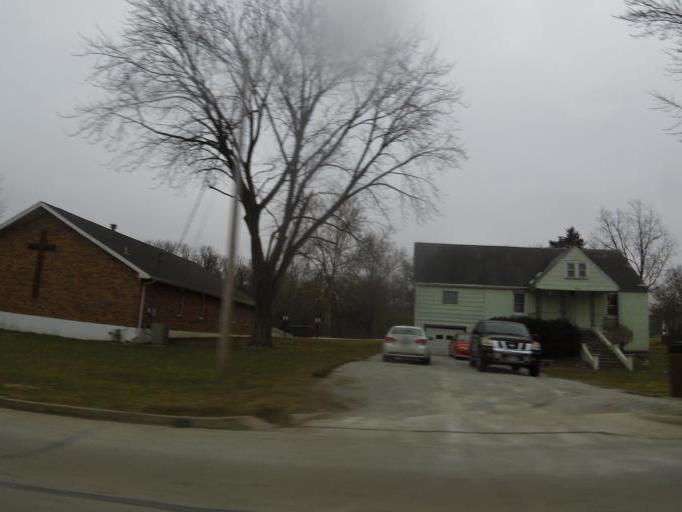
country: US
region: Missouri
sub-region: Marion County
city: Hannibal
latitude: 39.7131
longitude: -91.3988
